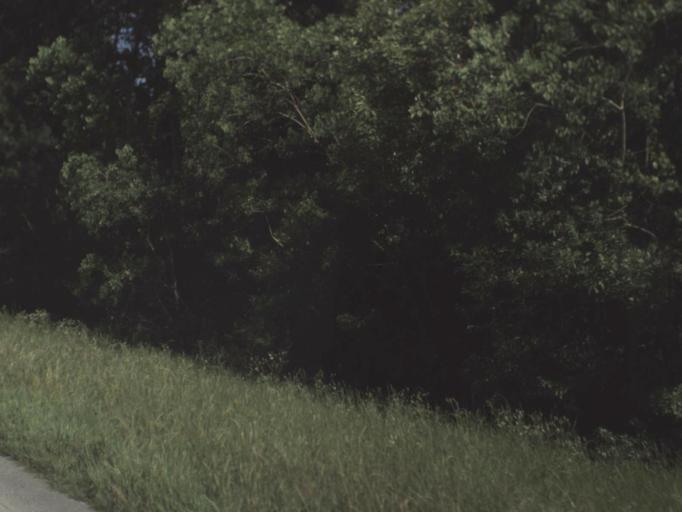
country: US
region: Florida
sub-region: Duval County
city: Baldwin
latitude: 30.3082
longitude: -81.9055
